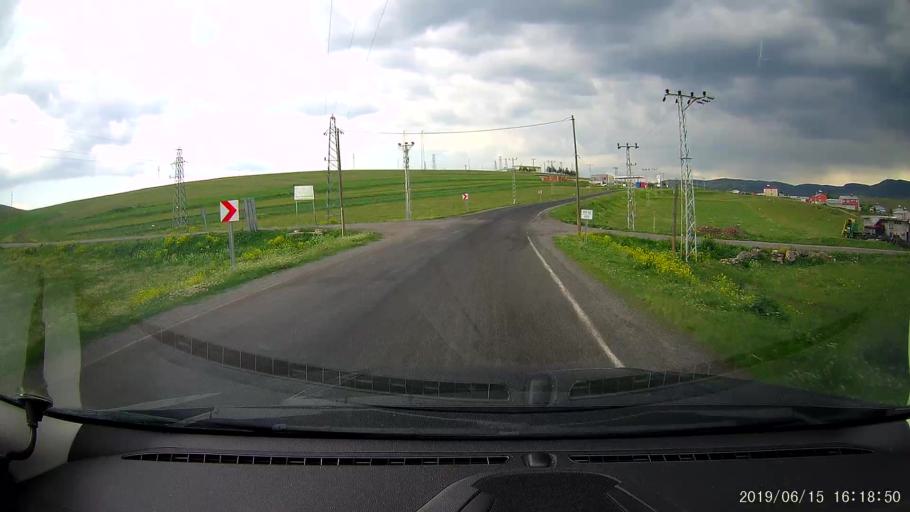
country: TR
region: Ardahan
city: Hanak
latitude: 41.2350
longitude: 42.8529
